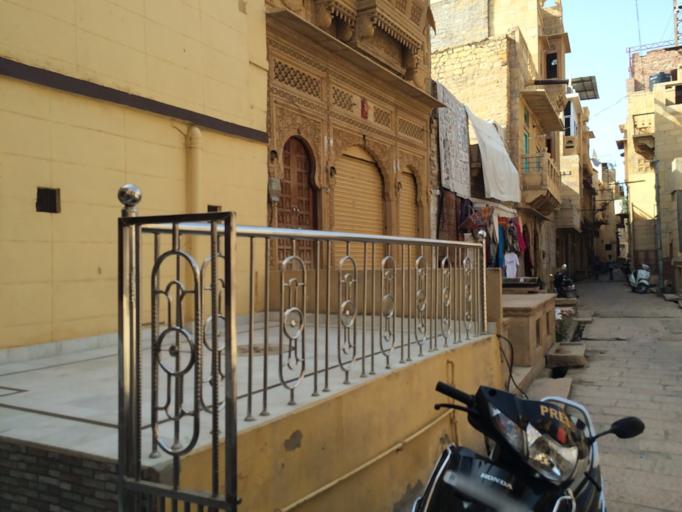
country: IN
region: Rajasthan
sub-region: Jaisalmer
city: Jaisalmer
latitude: 26.9159
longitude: 70.9125
